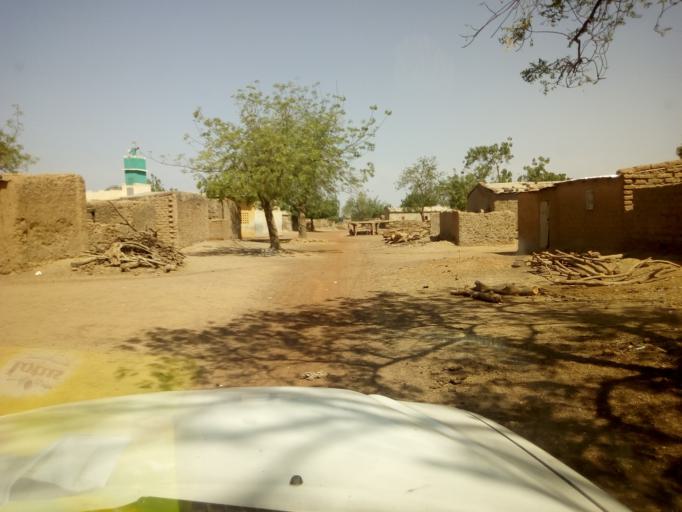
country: ML
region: Koulikoro
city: Koulikoro
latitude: 12.6488
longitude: -7.7104
